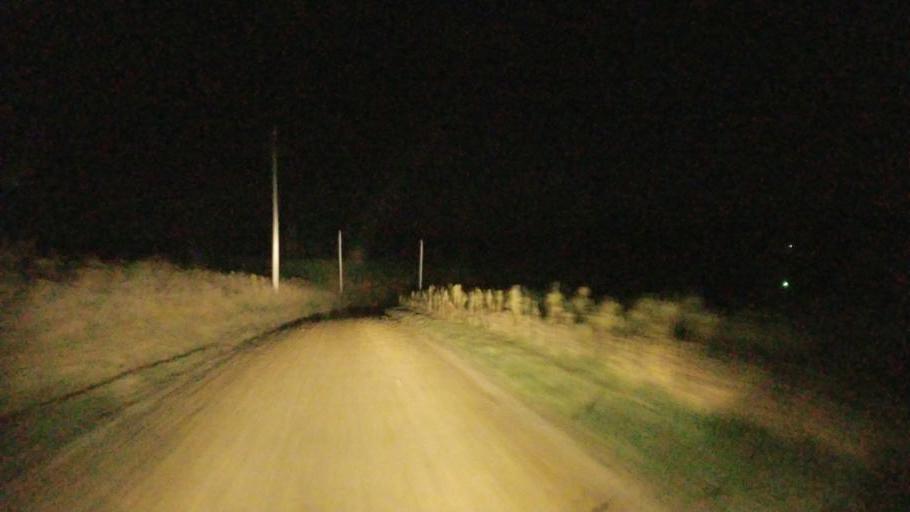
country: US
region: Ohio
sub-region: Knox County
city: Danville
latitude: 40.5461
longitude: -82.3516
